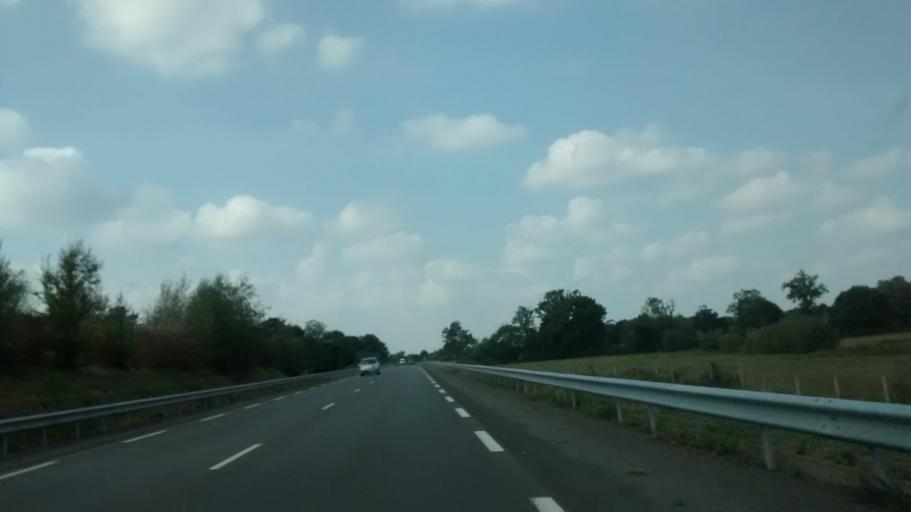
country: FR
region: Brittany
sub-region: Departement d'Ille-et-Vilaine
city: Saint-Aubin-du-Cormier
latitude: 48.2418
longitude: -1.3805
